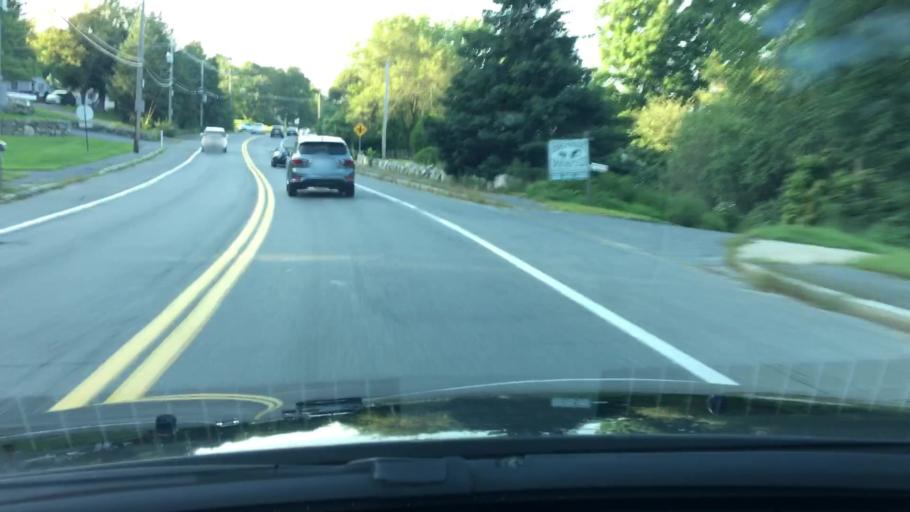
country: US
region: Massachusetts
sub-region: Worcester County
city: Shrewsbury
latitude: 42.3157
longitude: -71.7173
